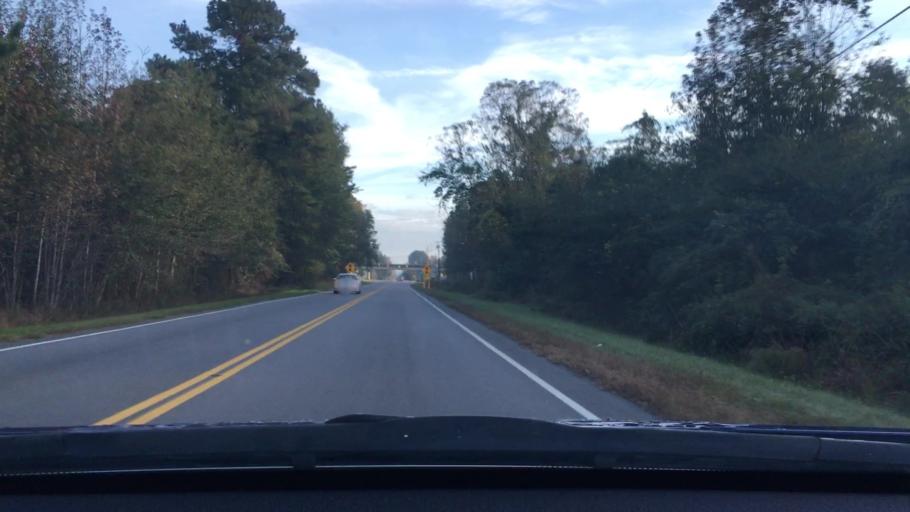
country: US
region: South Carolina
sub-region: Sumter County
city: Sumter
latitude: 33.9342
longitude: -80.3215
